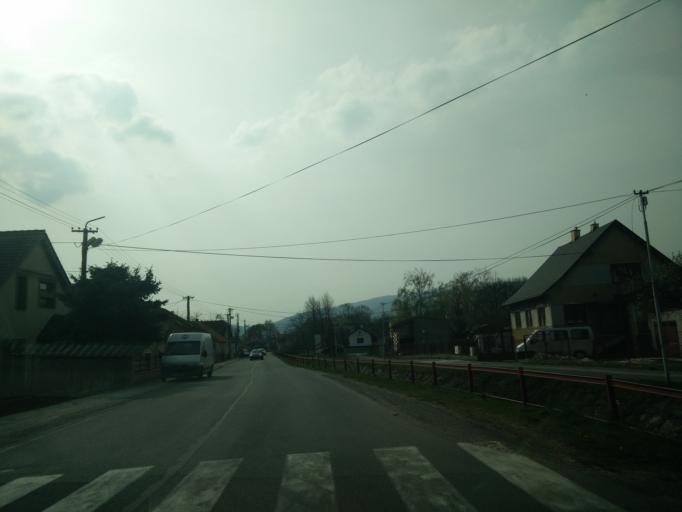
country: SK
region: Nitriansky
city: Prievidza
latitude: 48.8155
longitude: 18.6477
